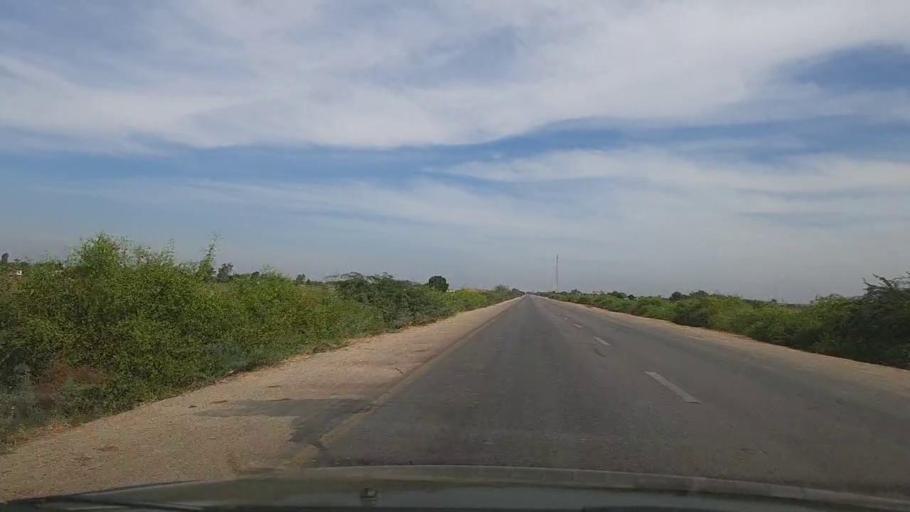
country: PK
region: Sindh
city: Thatta
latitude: 24.8060
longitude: 67.9708
